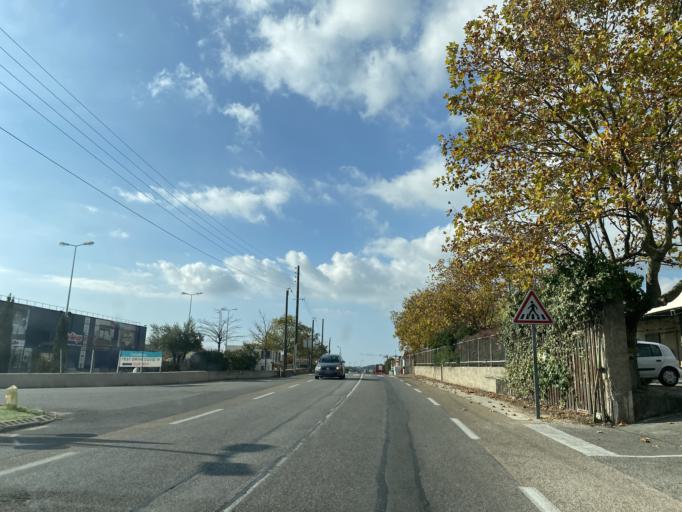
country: FR
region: Provence-Alpes-Cote d'Azur
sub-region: Departement du Var
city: Ollioules
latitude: 43.1276
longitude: 5.8605
